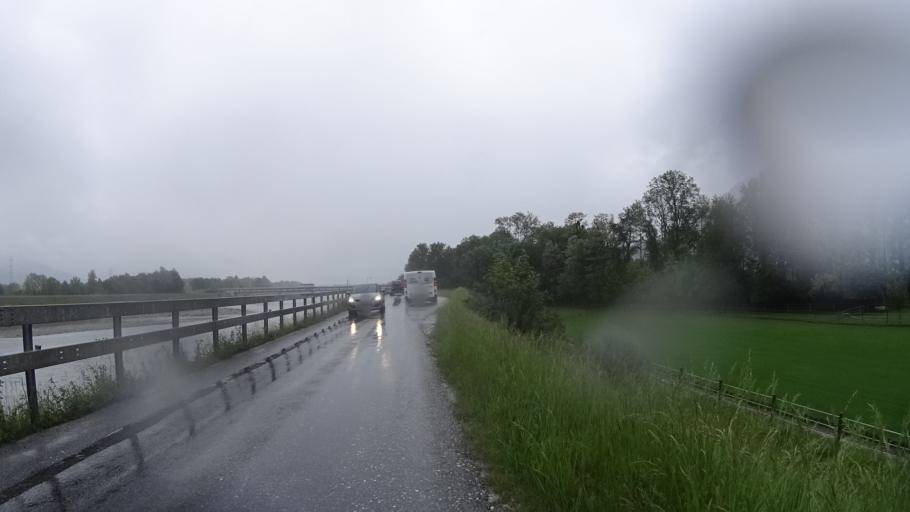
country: LI
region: Vaduz
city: Vaduz
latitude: 47.1264
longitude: 9.5144
